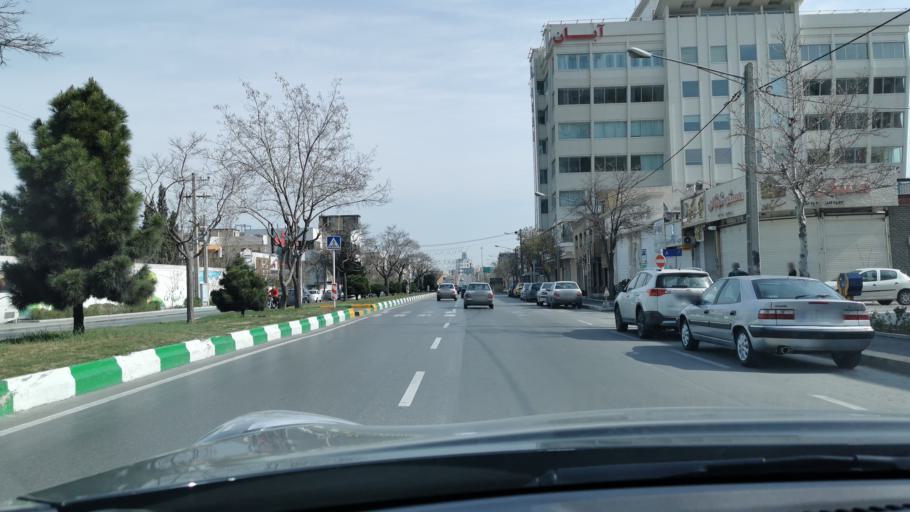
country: IR
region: Razavi Khorasan
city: Mashhad
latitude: 36.3196
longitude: 59.5125
